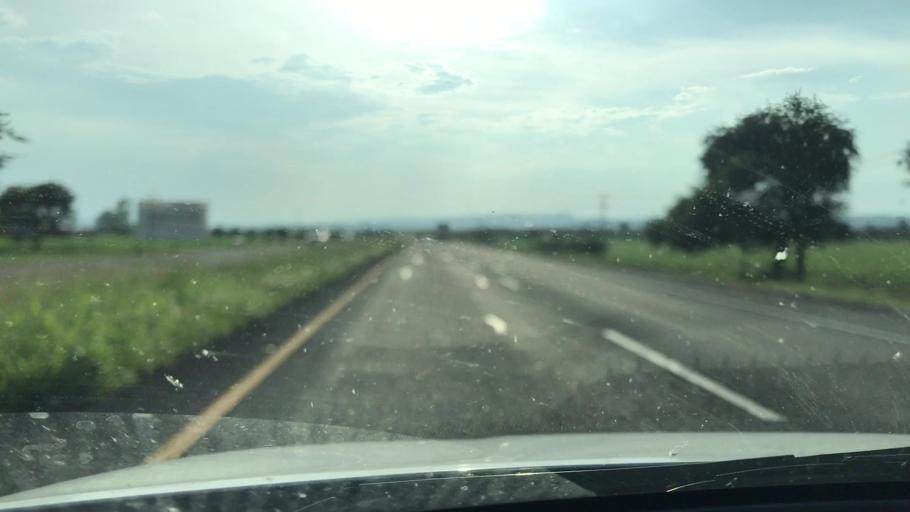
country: MX
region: Guanajuato
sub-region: Penjamo
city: Mezquite de Luna
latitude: 20.3835
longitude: -101.8813
